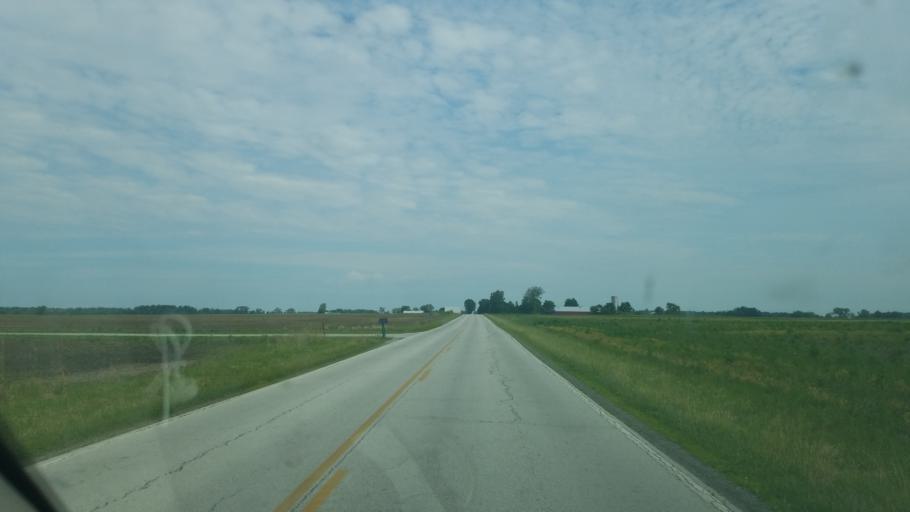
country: US
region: Ohio
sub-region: Seneca County
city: Fostoria
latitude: 41.0804
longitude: -83.4783
